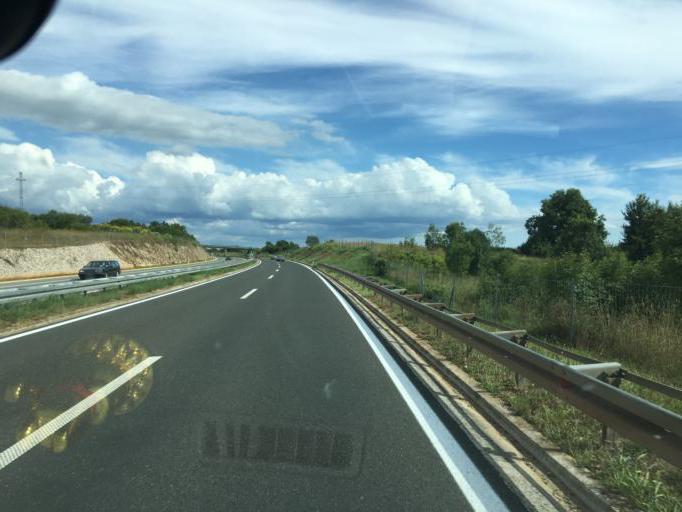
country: HR
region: Istarska
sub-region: Grad Rovinj
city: Rovinj
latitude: 45.1310
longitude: 13.7699
